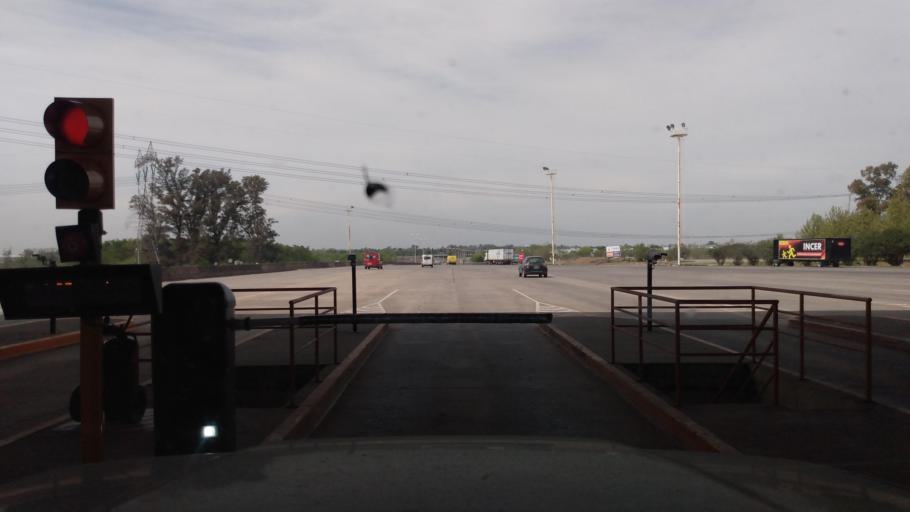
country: AR
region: Buenos Aires
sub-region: Partido de Pilar
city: Pilar
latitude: -34.4031
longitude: -59.0140
